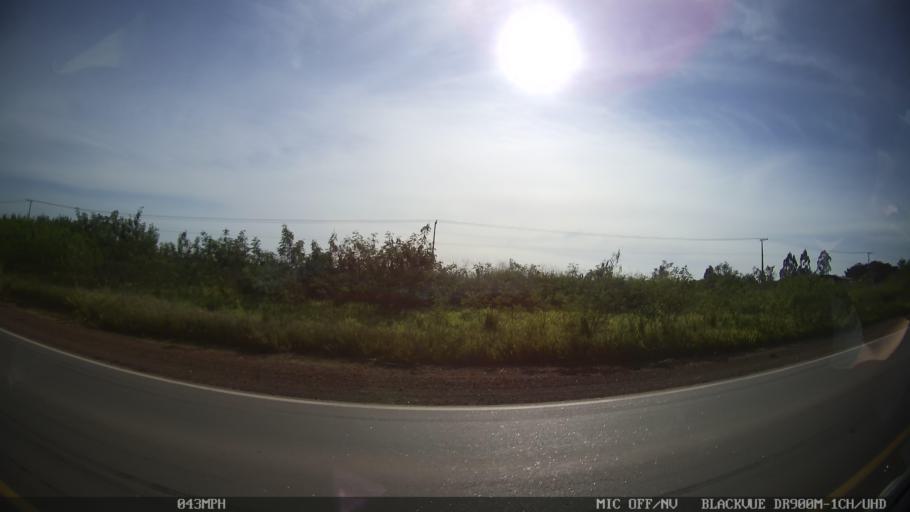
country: BR
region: Sao Paulo
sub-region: Rio Das Pedras
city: Rio das Pedras
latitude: -22.7926
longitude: -47.6226
